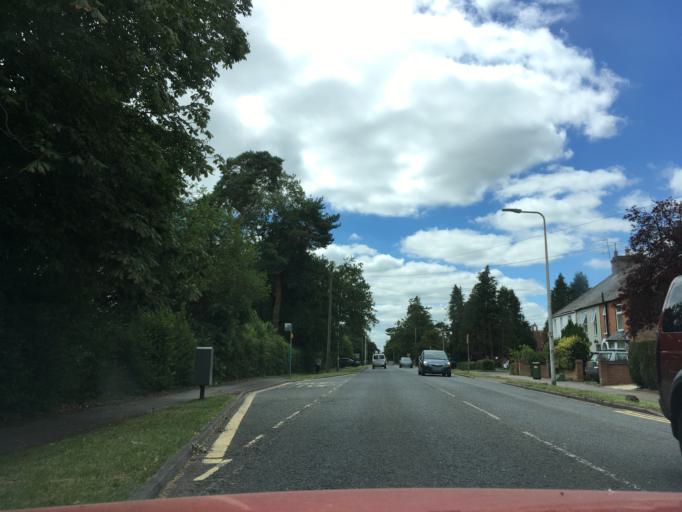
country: GB
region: England
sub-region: West Berkshire
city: Newbury
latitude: 51.3795
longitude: -1.3420
